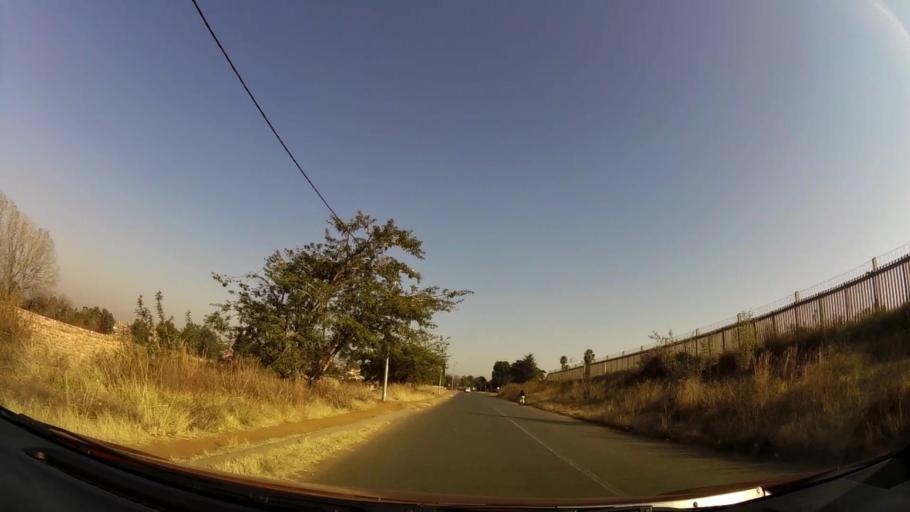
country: ZA
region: Gauteng
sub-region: City of Johannesburg Metropolitan Municipality
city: Soweto
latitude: -26.2953
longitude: 27.9554
